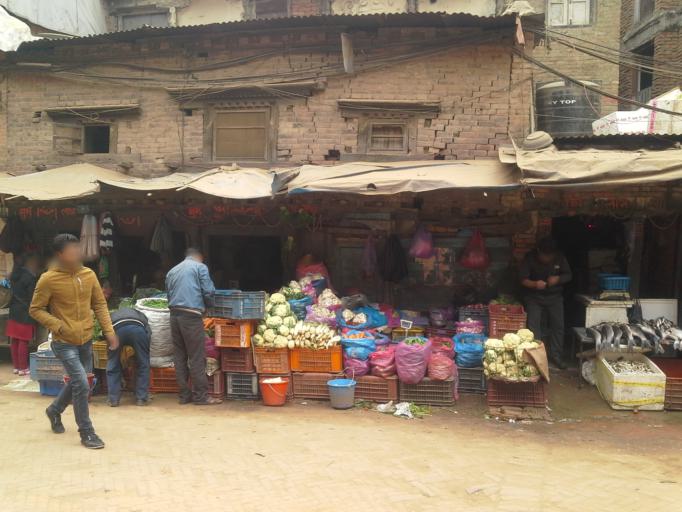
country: NP
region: Central Region
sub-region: Bagmati Zone
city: Bhaktapur
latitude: 27.6726
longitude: 85.4311
